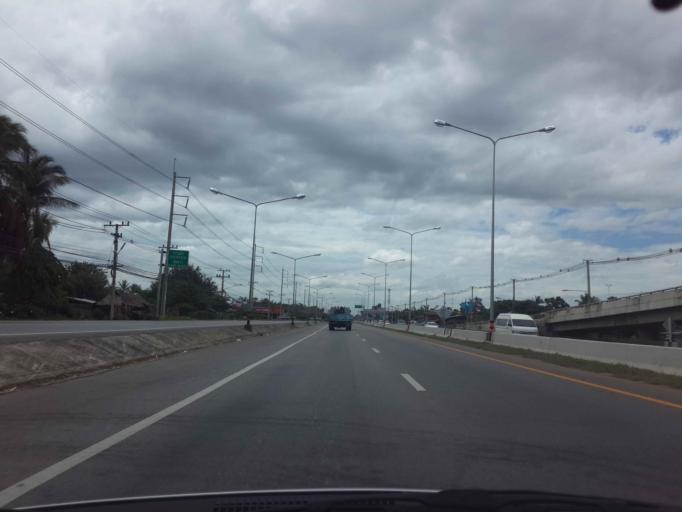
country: TH
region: Phetchaburi
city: Phetchaburi
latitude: 13.1447
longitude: 99.8564
